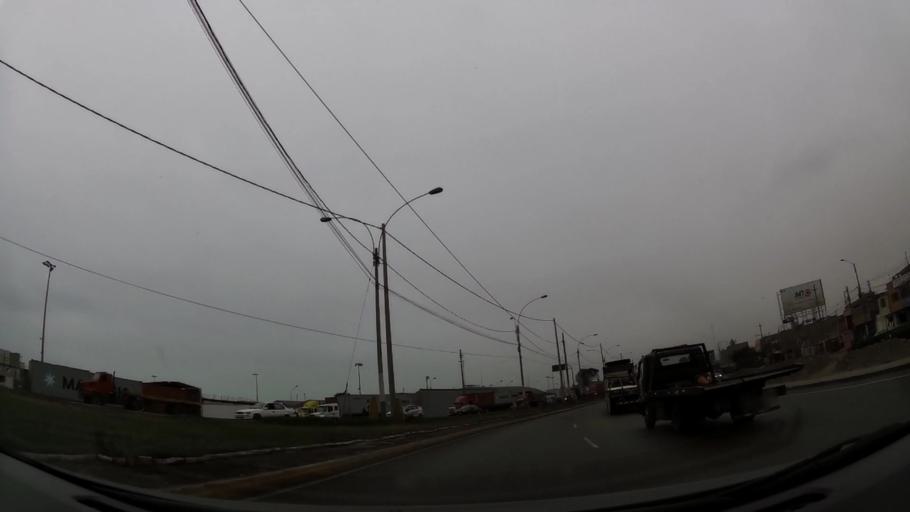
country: PE
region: Callao
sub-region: Callao
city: Callao
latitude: -11.9958
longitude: -77.1260
